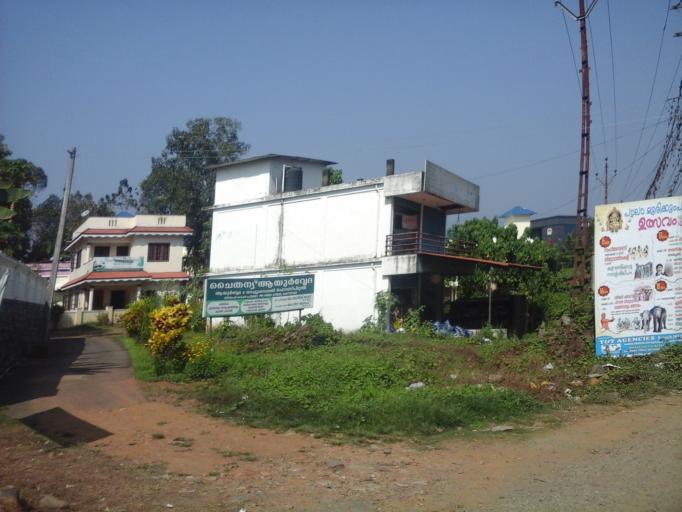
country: IN
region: Kerala
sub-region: Kottayam
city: Lalam
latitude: 9.7078
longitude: 76.6833
